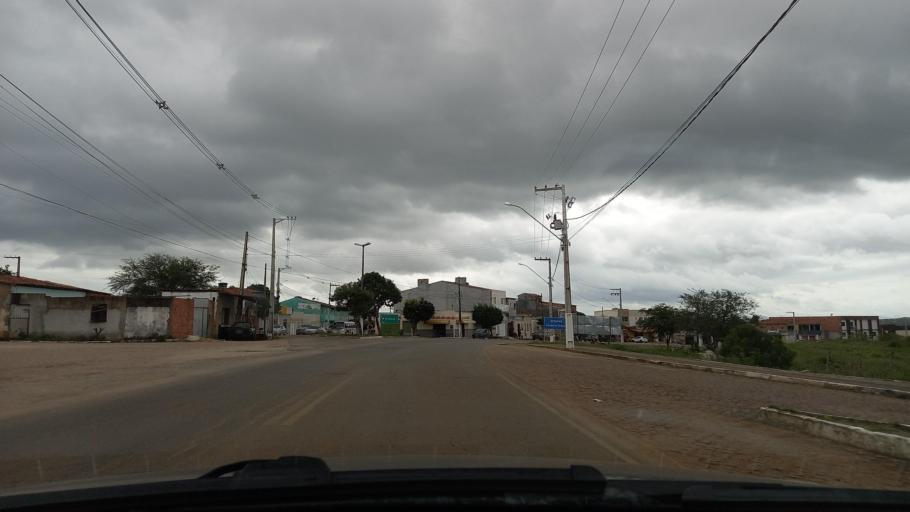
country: BR
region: Sergipe
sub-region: Caninde De Sao Francisco
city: Caninde de Sao Francisco
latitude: -9.6668
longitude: -37.7965
